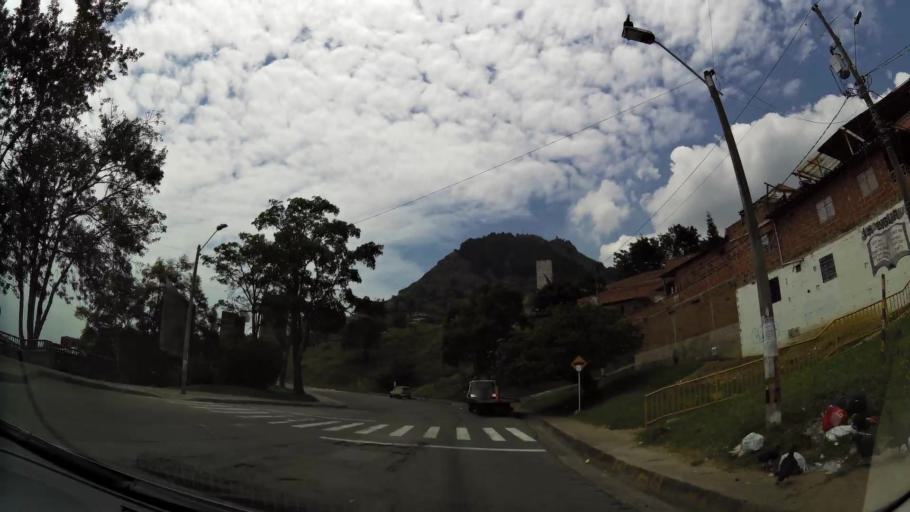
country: CO
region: Antioquia
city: Bello
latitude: 6.3070
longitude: -75.5814
